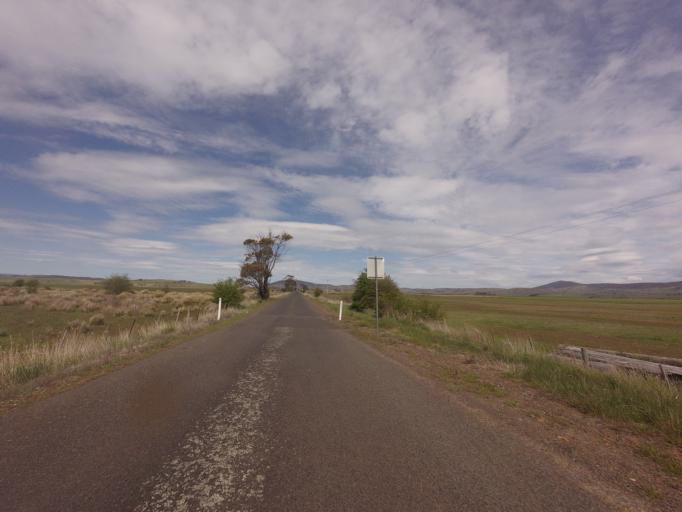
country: AU
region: Tasmania
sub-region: Northern Midlands
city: Evandale
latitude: -41.8645
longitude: 147.3484
